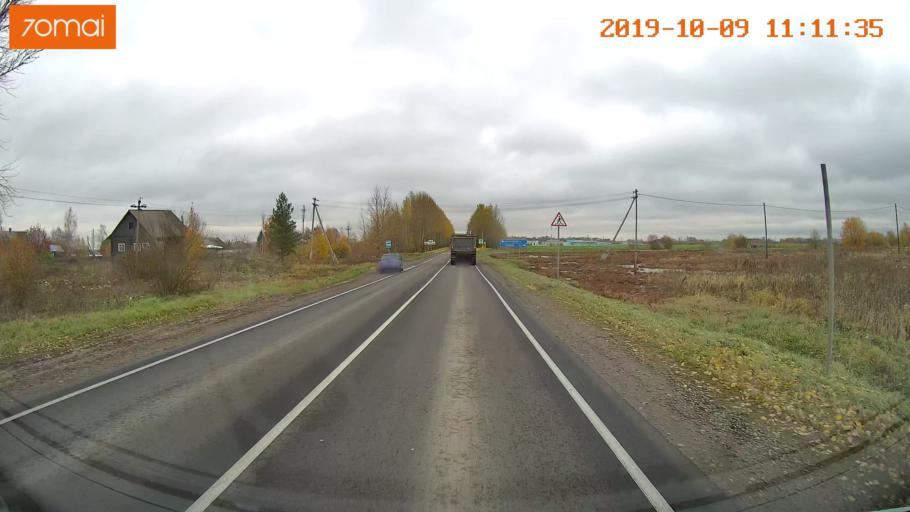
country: RU
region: Vologda
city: Vologda
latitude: 59.1694
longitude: 39.8220
